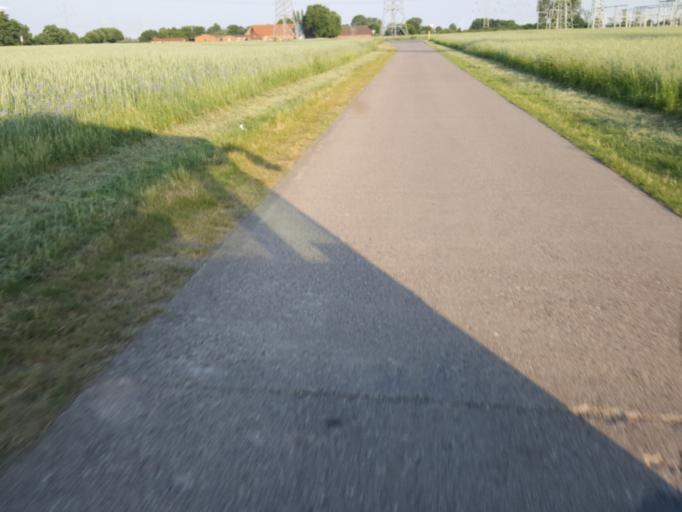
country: DE
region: Lower Saxony
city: Landesbergen
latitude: 52.5412
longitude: 9.1189
